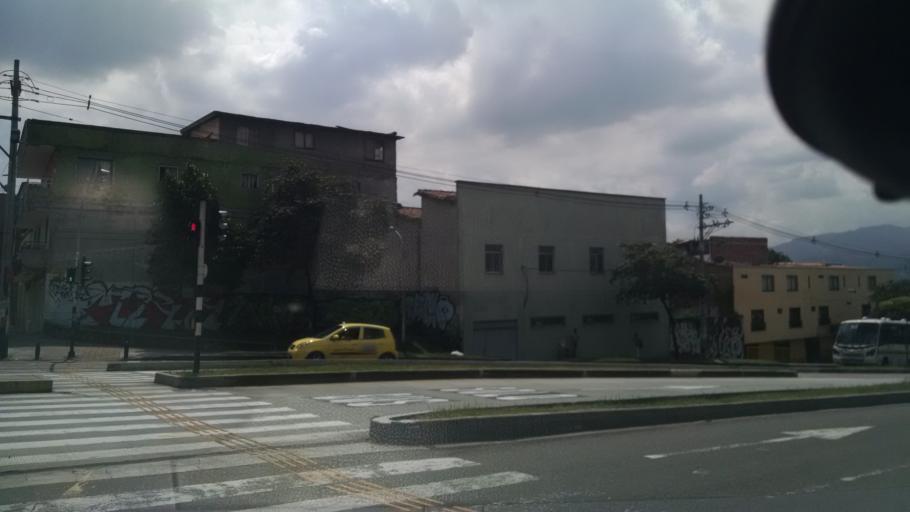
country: CO
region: Antioquia
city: Medellin
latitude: 6.2636
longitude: -75.5605
